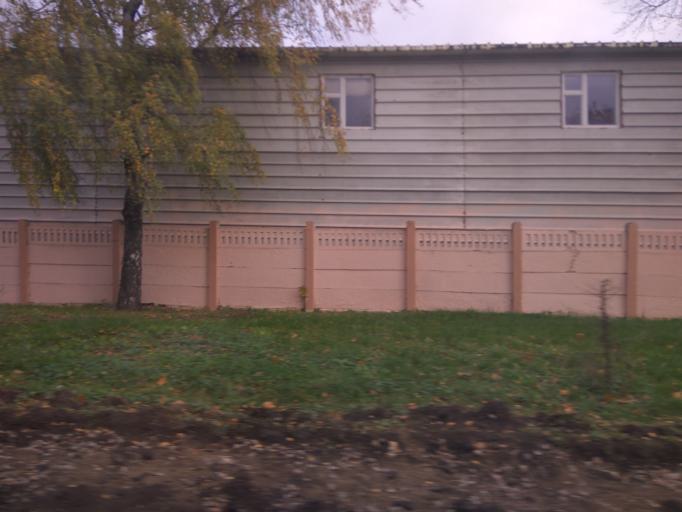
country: RU
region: Moscow
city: Tsaritsyno
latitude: 55.6325
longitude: 37.6400
